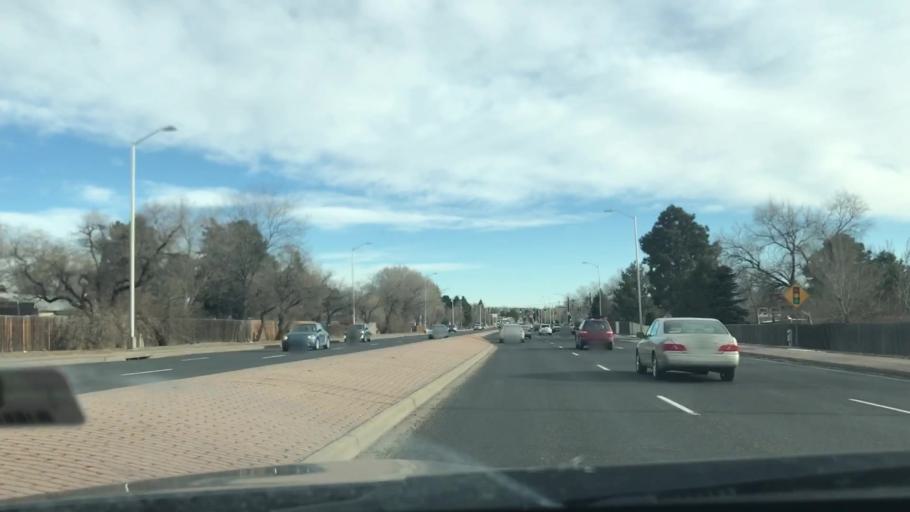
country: US
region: Colorado
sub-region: El Paso County
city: Cimarron Hills
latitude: 38.8991
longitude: -104.7635
